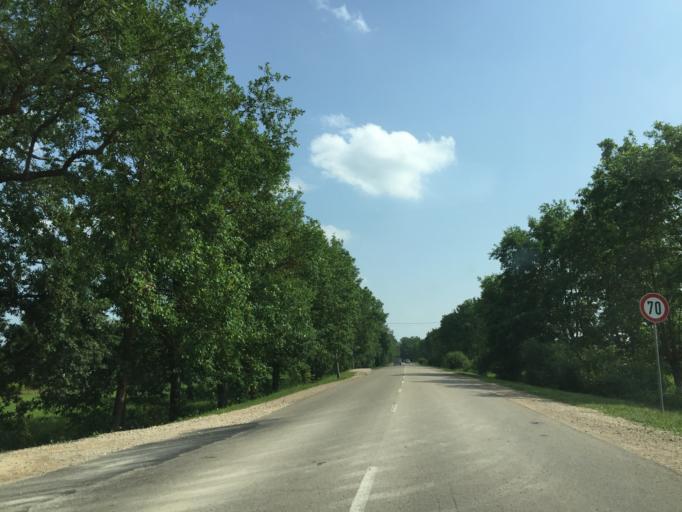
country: LV
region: Jelgava
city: Jelgava
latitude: 56.6784
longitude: 23.7236
